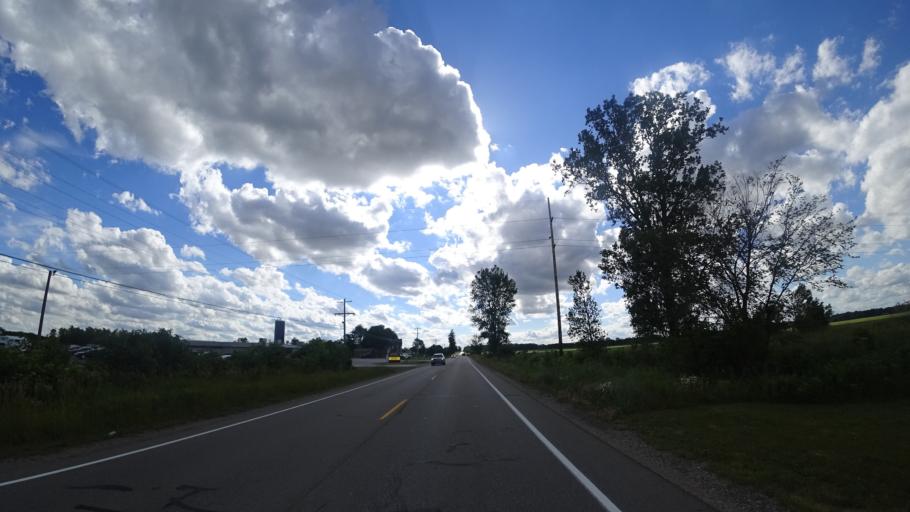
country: US
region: Michigan
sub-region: Ionia County
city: Portland
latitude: 42.8716
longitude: -84.9252
